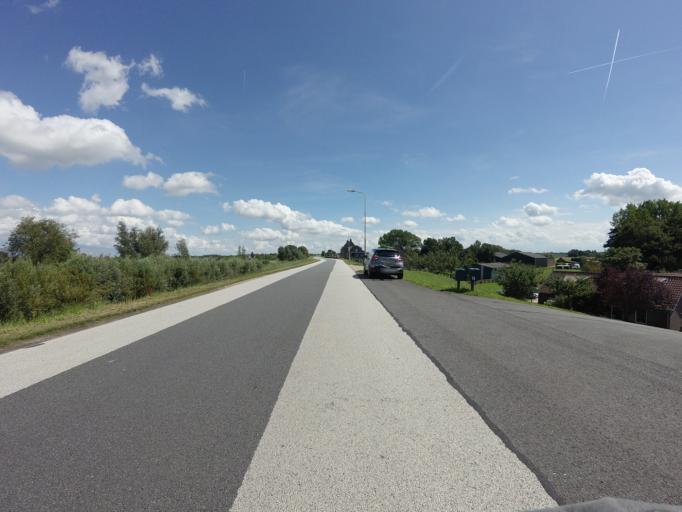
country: NL
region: Utrecht
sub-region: Gemeente Lopik
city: Lopik
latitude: 51.9574
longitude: 4.9676
